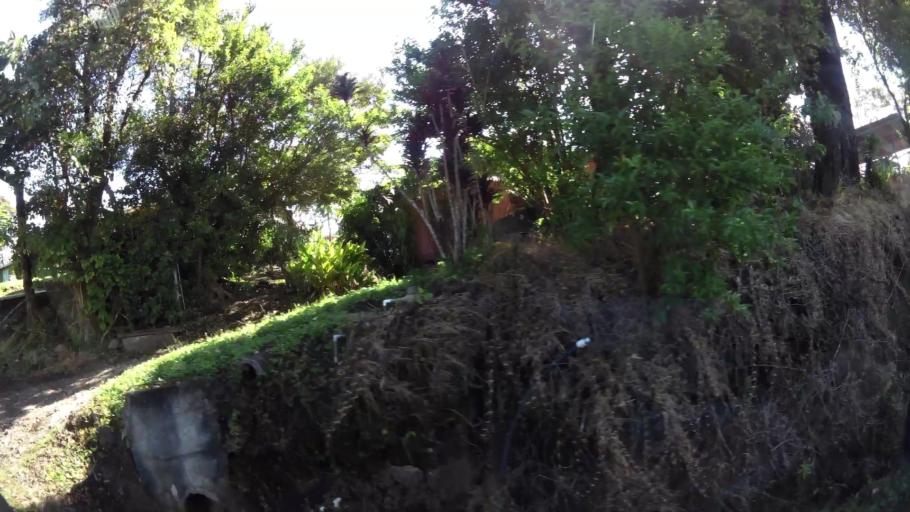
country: CR
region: Guanacaste
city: Juntas
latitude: 10.3207
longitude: -84.8241
